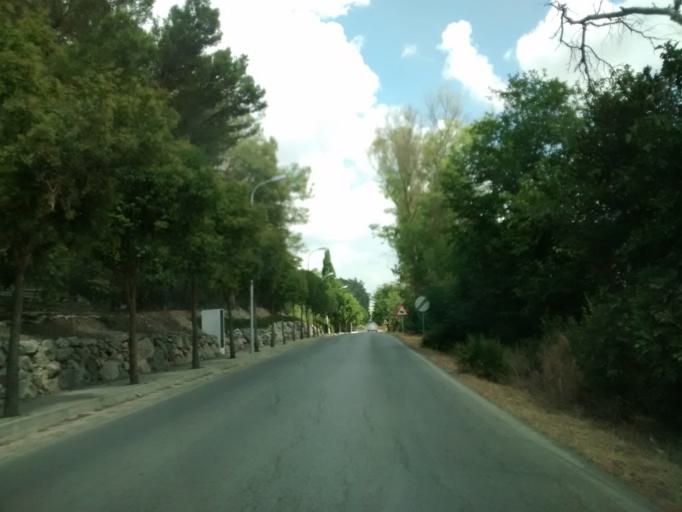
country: ES
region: Andalusia
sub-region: Provincia de Cadiz
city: Arcos de la Frontera
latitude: 36.6991
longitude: -5.8582
